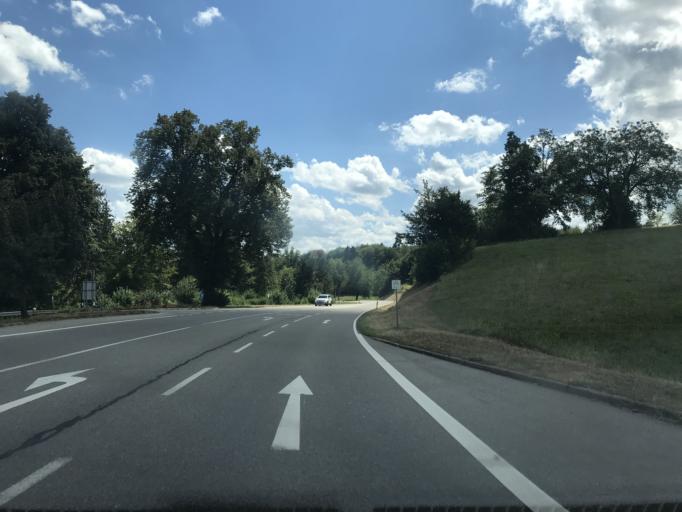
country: DE
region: Baden-Wuerttemberg
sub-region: Freiburg Region
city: Hasel
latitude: 47.6479
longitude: 7.8882
